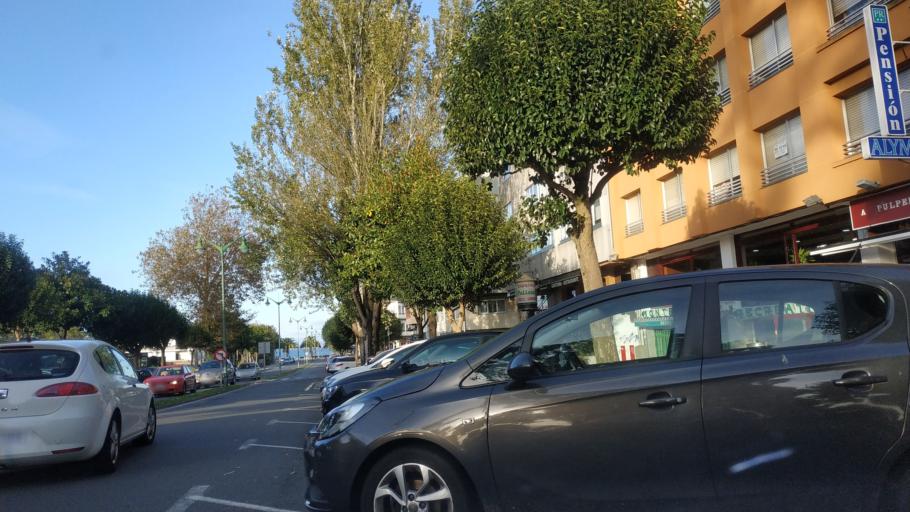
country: ES
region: Galicia
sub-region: Provincia da Coruna
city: A Coruna
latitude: 43.3369
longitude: -8.3773
